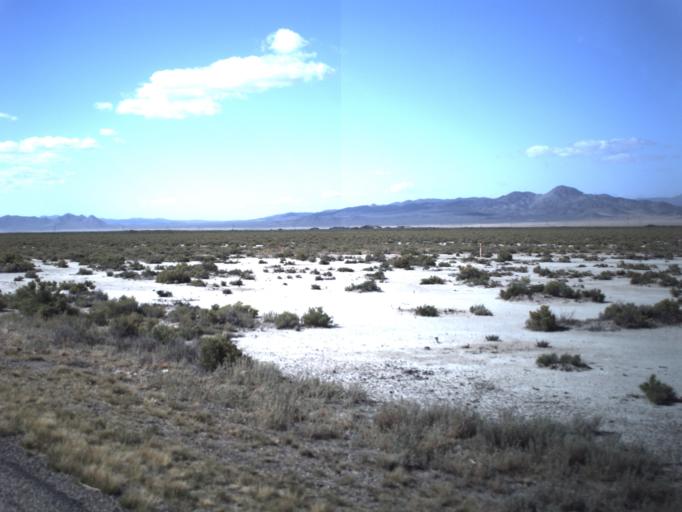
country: US
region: Utah
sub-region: Beaver County
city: Milford
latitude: 38.6023
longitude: -112.9872
